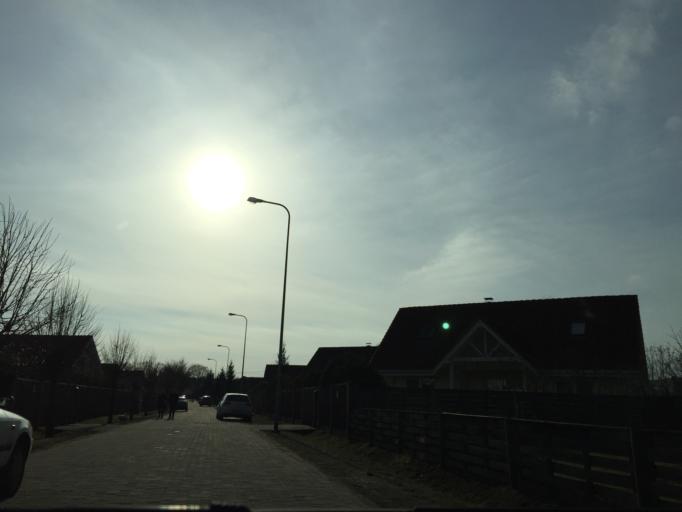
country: LV
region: Stopini
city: Ulbroka
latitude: 56.9290
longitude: 24.2592
